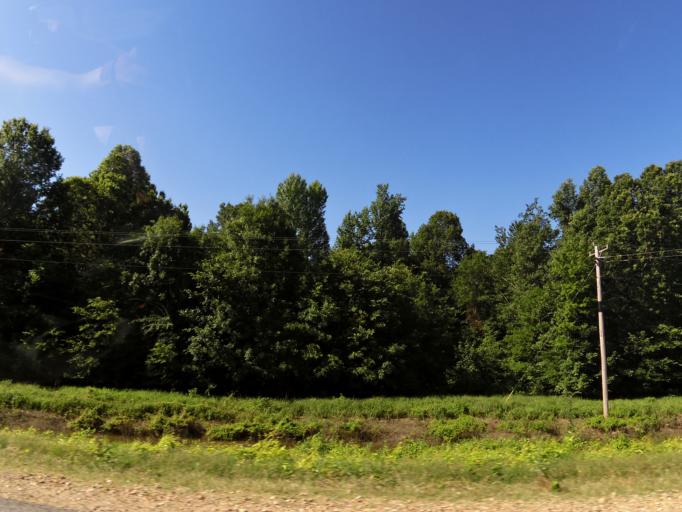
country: US
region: Arkansas
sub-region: Clay County
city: Corning
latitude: 36.4005
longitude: -90.5377
